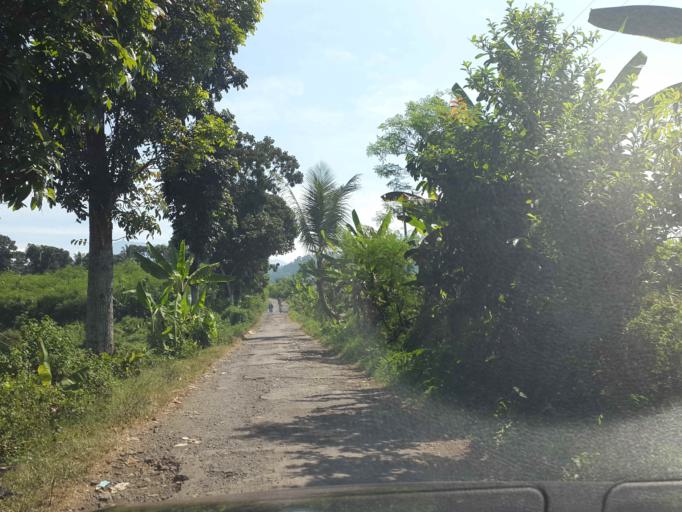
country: ID
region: West Java
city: Ciranjang-hilir
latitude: -6.7470
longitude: 107.1760
